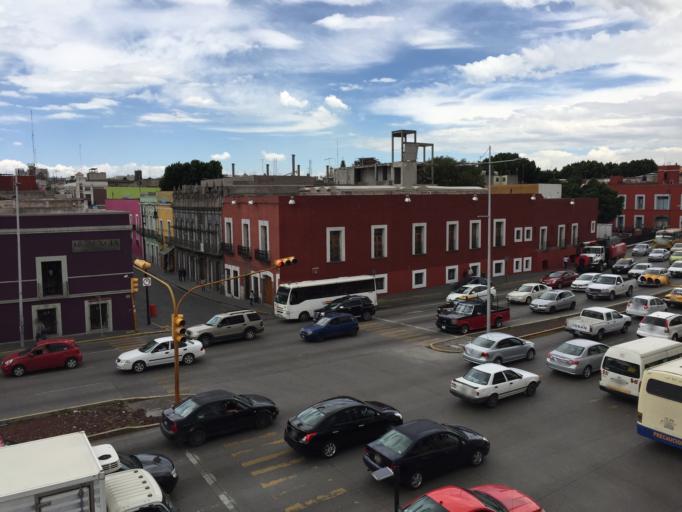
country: MX
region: Puebla
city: Puebla
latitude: 19.0421
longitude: -98.1922
